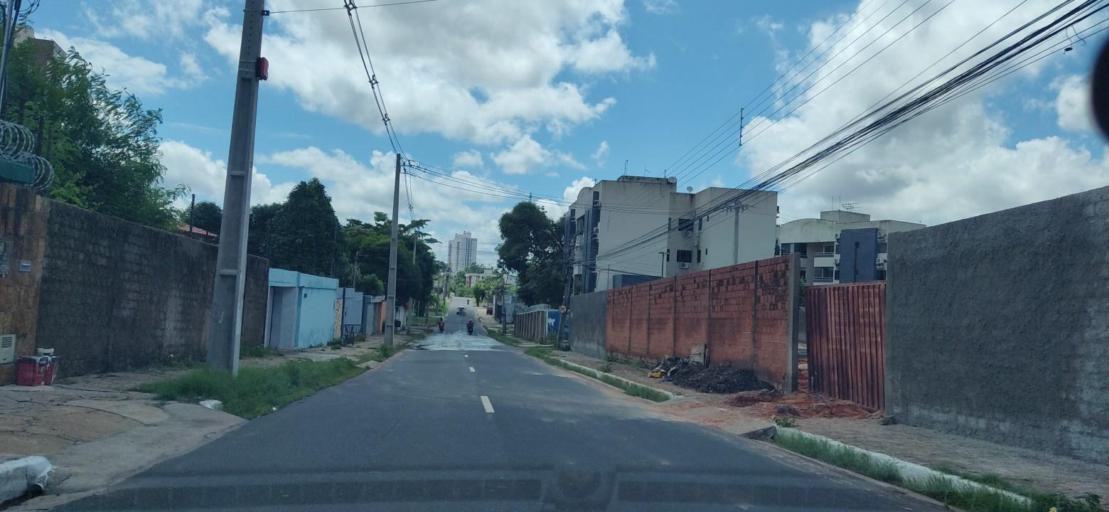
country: BR
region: Piaui
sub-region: Teresina
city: Teresina
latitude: -5.0655
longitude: -42.7786
